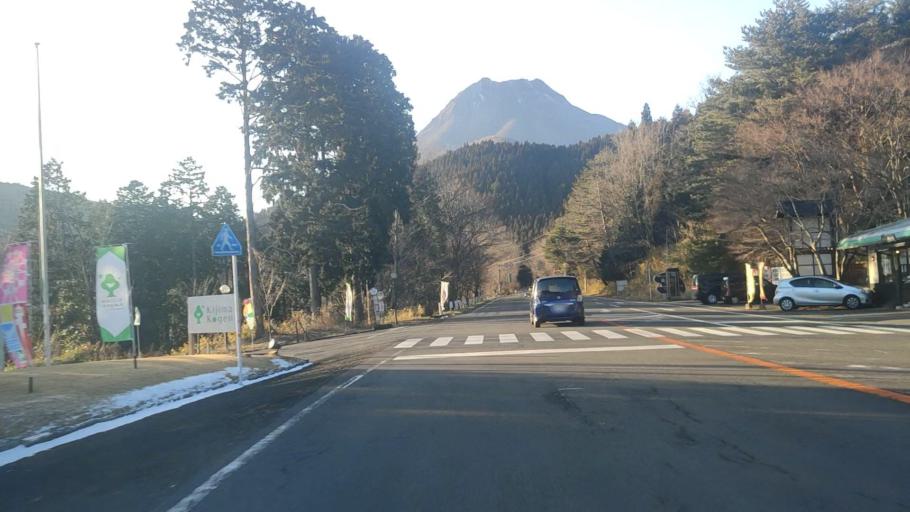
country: JP
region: Oita
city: Beppu
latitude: 33.2685
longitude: 131.4265
